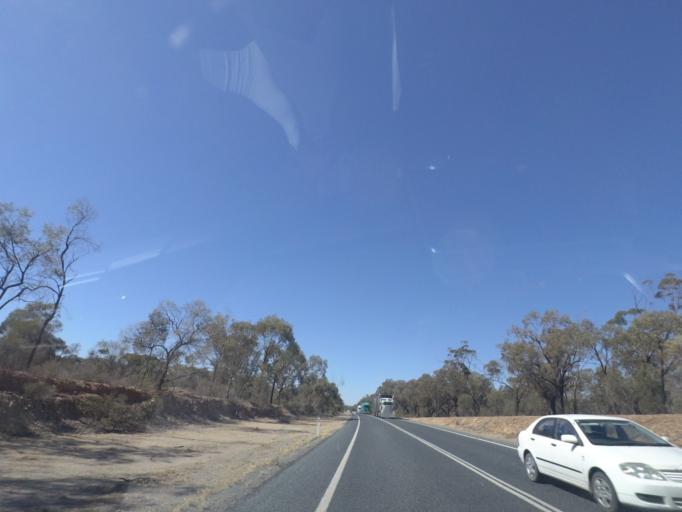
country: AU
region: New South Wales
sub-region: Bland
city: West Wyalong
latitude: -34.1391
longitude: 147.1206
